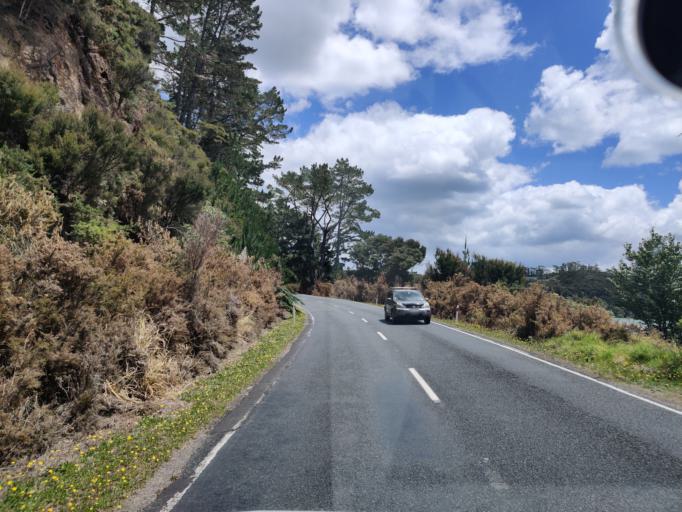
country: NZ
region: Northland
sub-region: Far North District
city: Paihia
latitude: -35.2905
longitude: 174.1420
